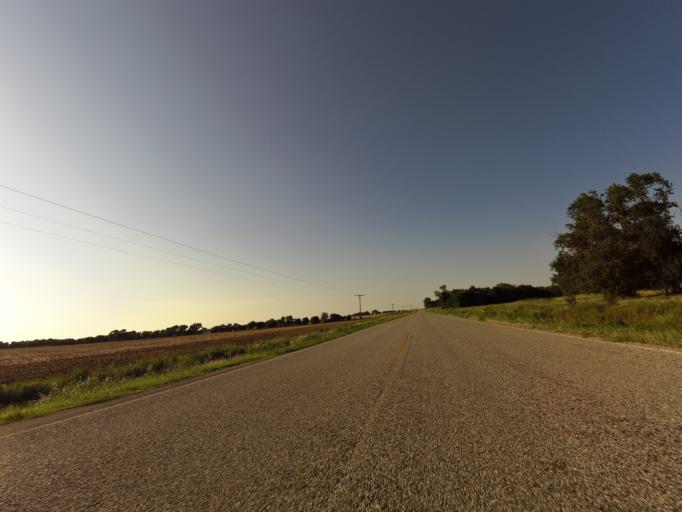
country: US
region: Kansas
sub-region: Reno County
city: Buhler
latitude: 38.1780
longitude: -97.8486
